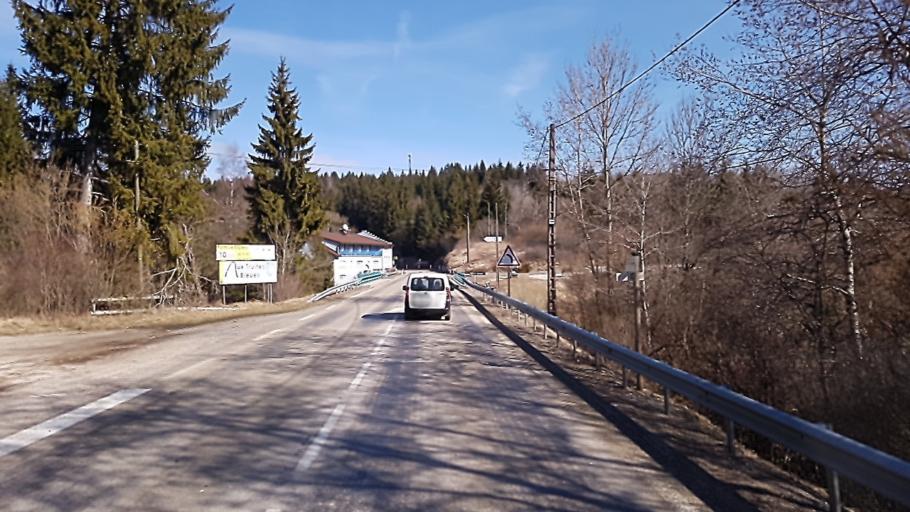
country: FR
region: Franche-Comte
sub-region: Departement du Jura
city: Morbier
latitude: 46.6203
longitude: 5.9602
